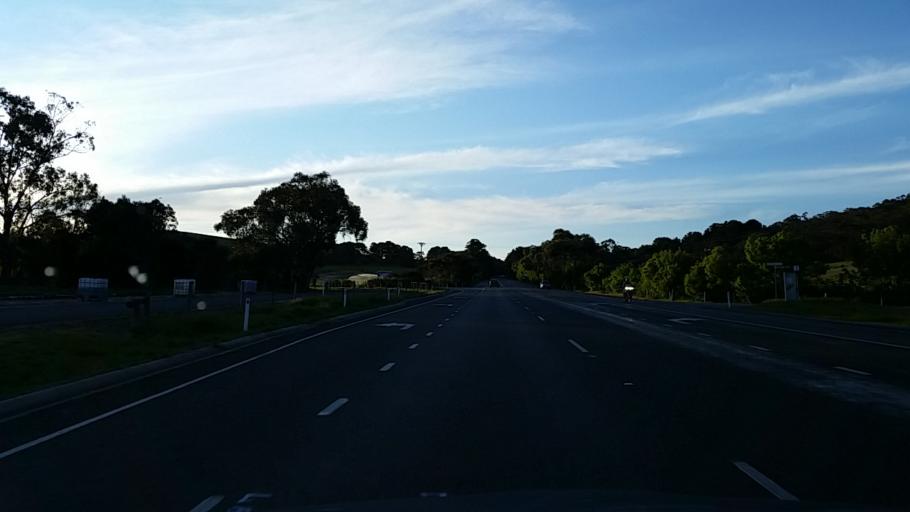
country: AU
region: South Australia
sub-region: Alexandrina
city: Mount Compass
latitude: -35.3409
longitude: 138.6000
